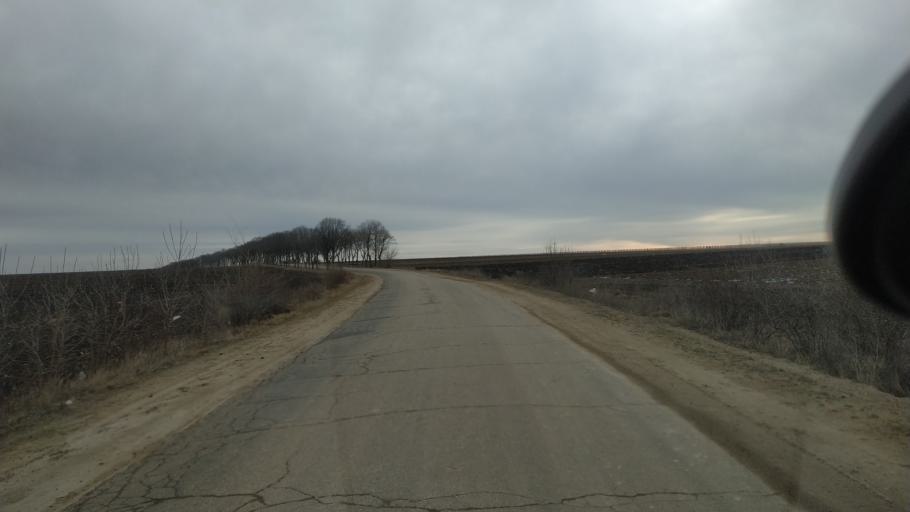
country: MD
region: Telenesti
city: Cocieri
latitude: 47.2667
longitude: 29.0828
